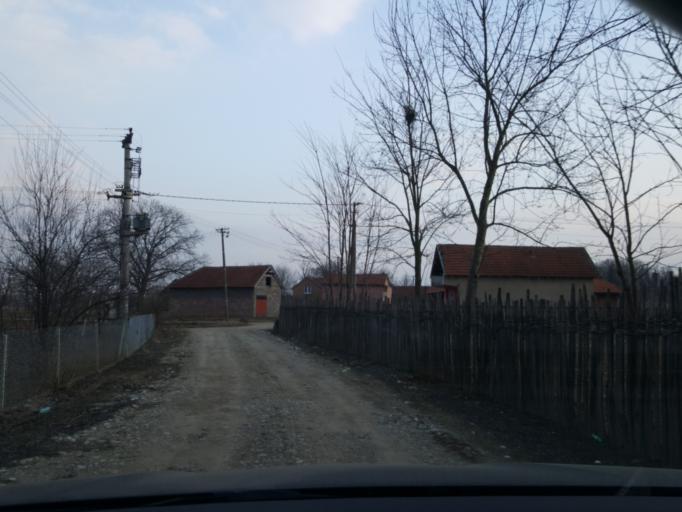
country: RS
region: Central Serbia
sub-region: Nisavski Okrug
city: Aleksinac
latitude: 43.5883
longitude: 21.6138
